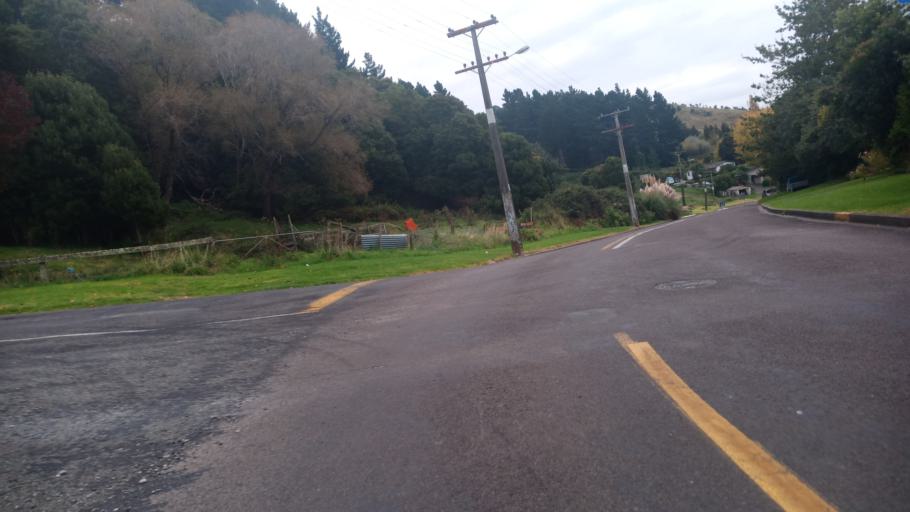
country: NZ
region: Gisborne
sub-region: Gisborne District
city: Gisborne
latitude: -38.6828
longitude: 178.0407
